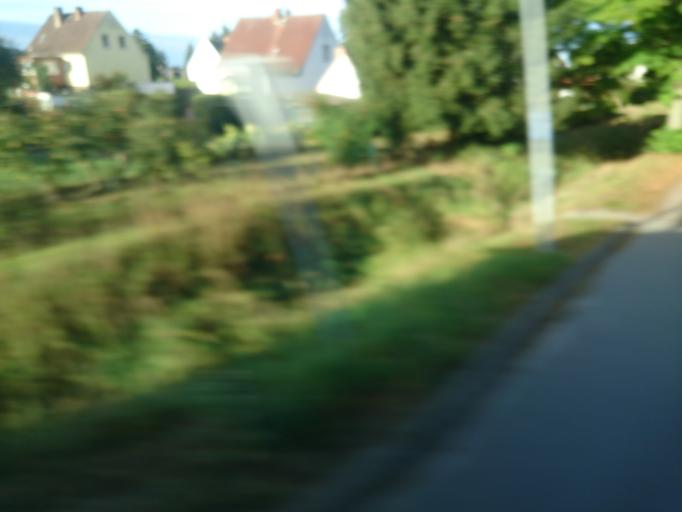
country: DE
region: Mecklenburg-Vorpommern
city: Zussow
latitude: 53.9850
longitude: 13.6058
